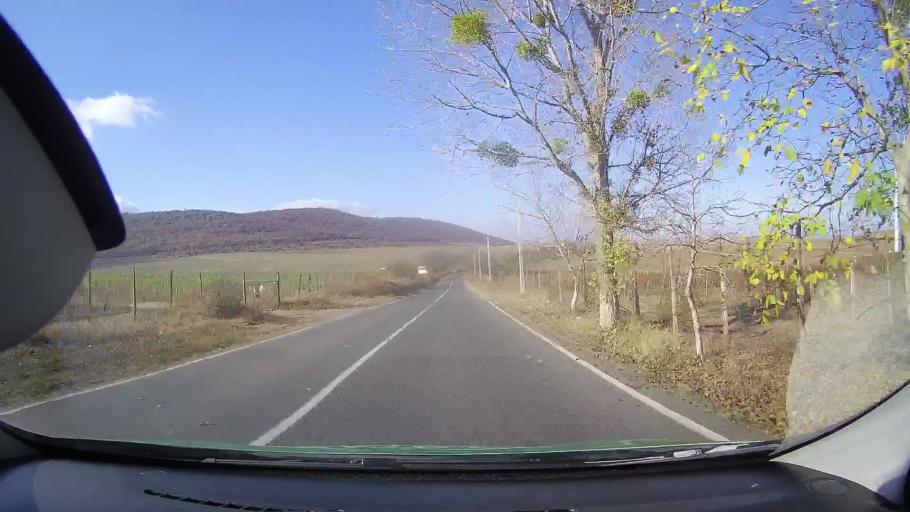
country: RO
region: Tulcea
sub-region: Oras Babadag
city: Babadag
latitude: 44.8801
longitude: 28.7494
